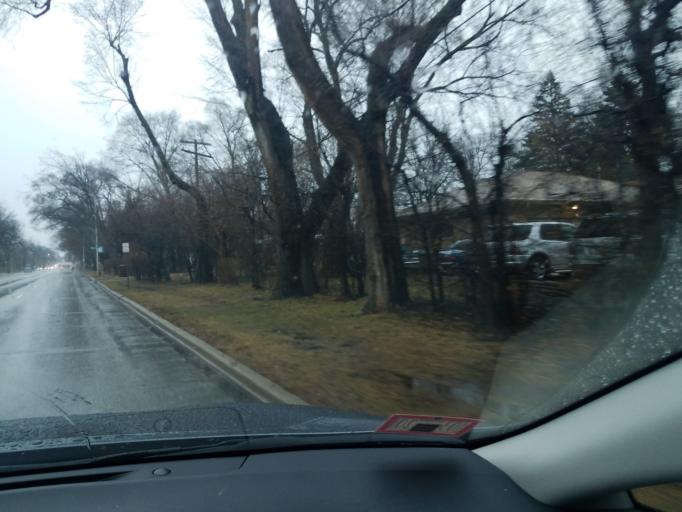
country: US
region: Illinois
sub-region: Cook County
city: Skokie
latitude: 42.0346
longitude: -87.7472
